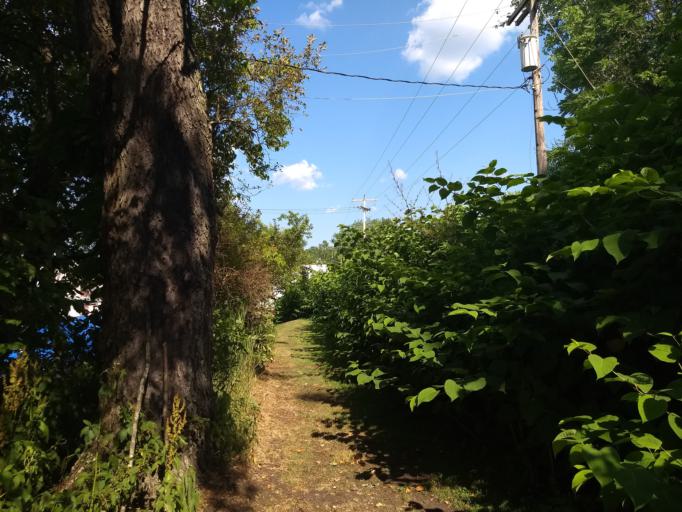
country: US
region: Pennsylvania
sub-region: Westmoreland County
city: Irwin
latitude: 40.3330
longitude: -79.7152
